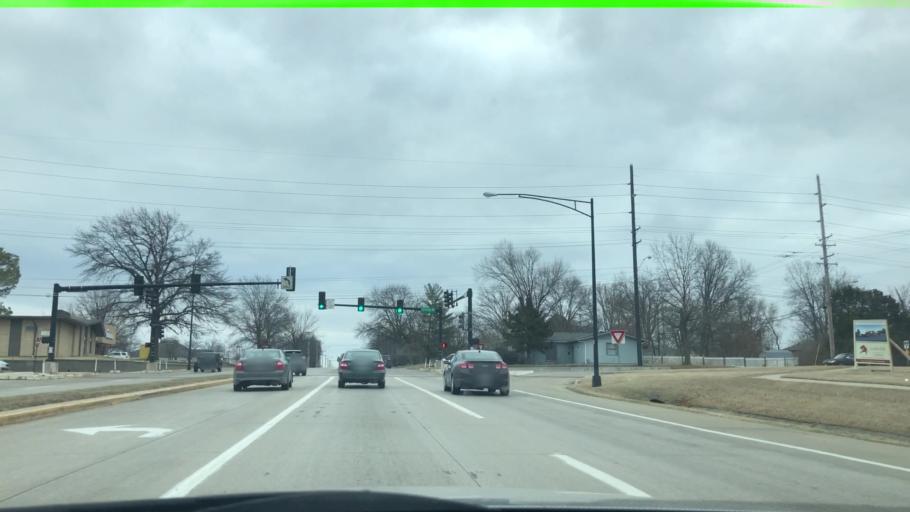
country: US
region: Missouri
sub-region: Boone County
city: Columbia
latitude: 38.9547
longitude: -92.3815
